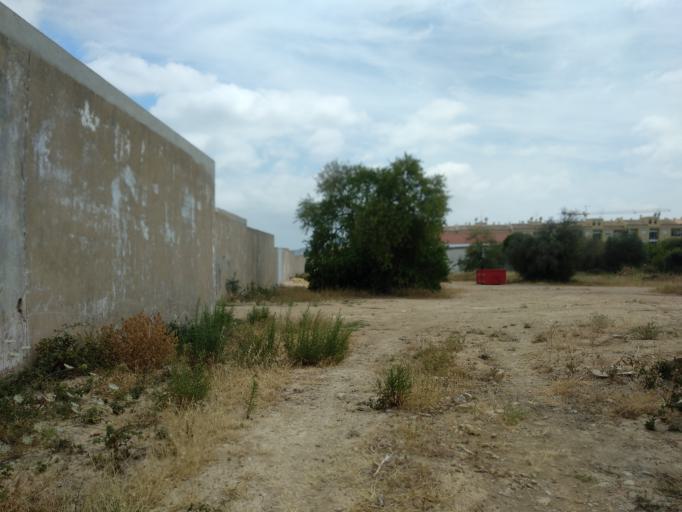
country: PT
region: Faro
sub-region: Sao Bras de Alportel
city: Sao Bras de Alportel
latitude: 37.1549
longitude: -7.8957
